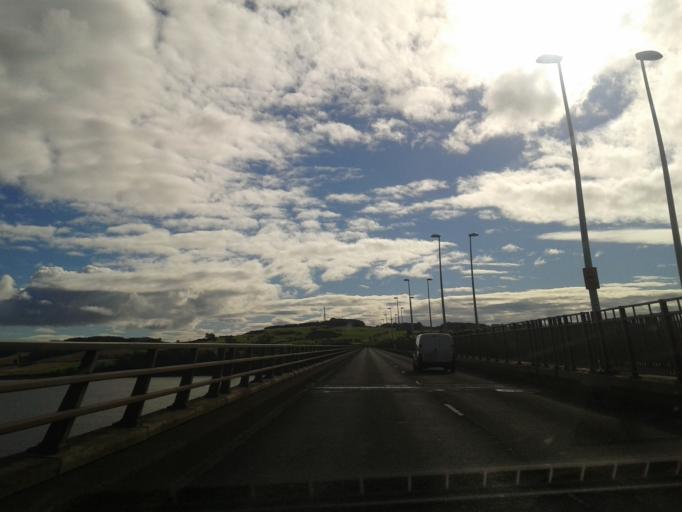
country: GB
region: Scotland
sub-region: Fife
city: Newport-On-Tay
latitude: 56.4530
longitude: -2.9479
